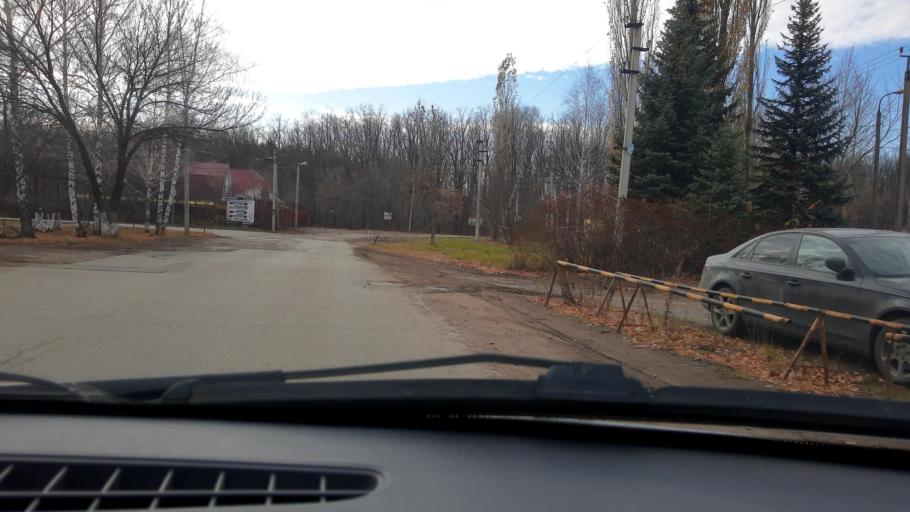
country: RU
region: Bashkortostan
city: Avdon
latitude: 54.6861
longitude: 55.7948
